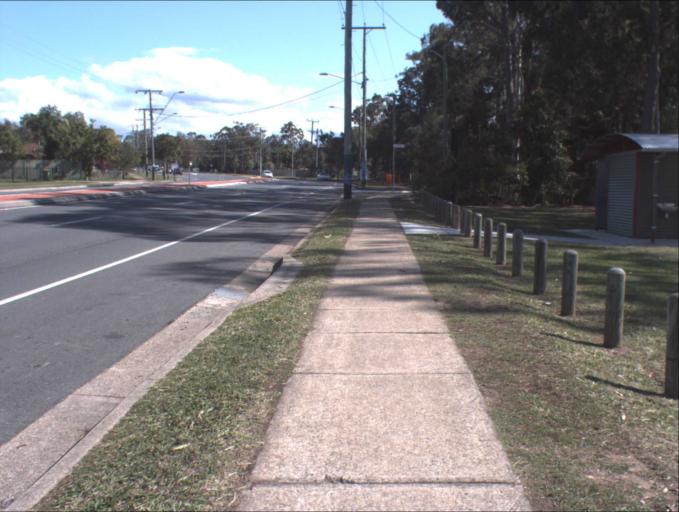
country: AU
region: Queensland
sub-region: Logan
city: Park Ridge South
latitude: -27.6801
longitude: 153.0196
